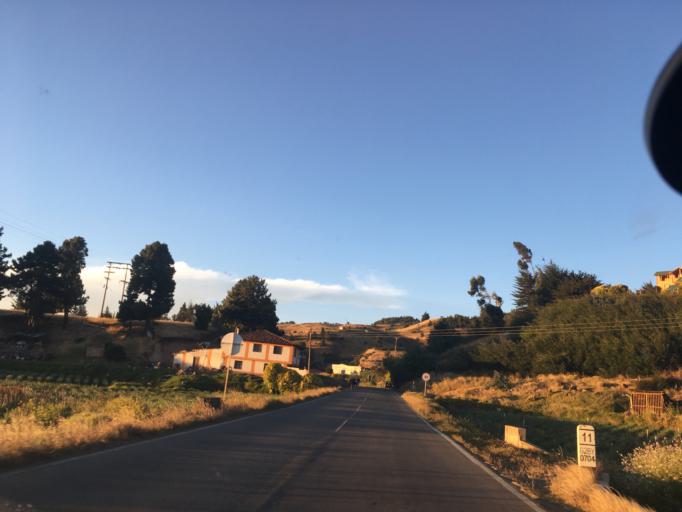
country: CO
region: Boyaca
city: Aquitania
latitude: 5.5588
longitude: -72.8802
